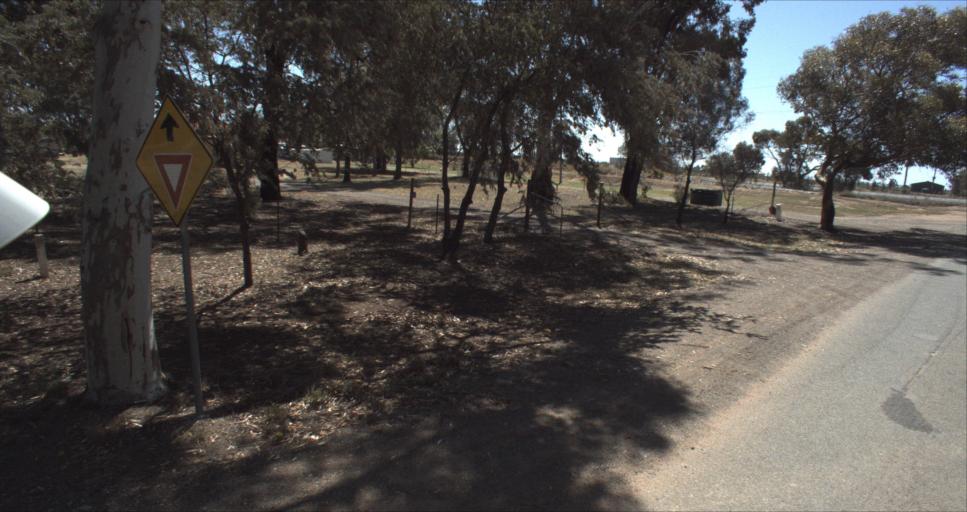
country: AU
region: New South Wales
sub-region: Leeton
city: Leeton
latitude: -34.5250
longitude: 146.3458
